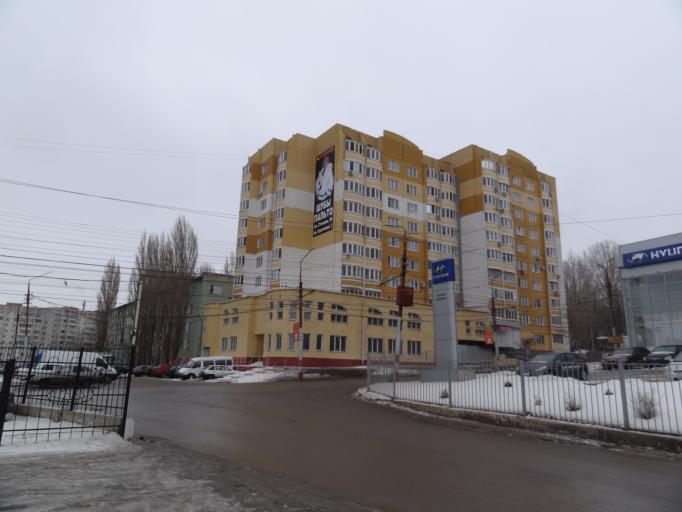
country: RU
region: Saratov
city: Engel's
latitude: 51.4838
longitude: 46.1249
